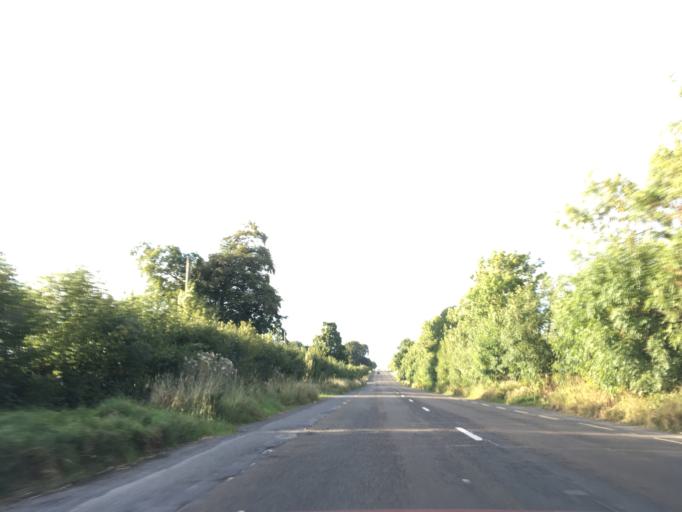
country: IE
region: Munster
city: Cashel
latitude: 52.4849
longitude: -7.8914
